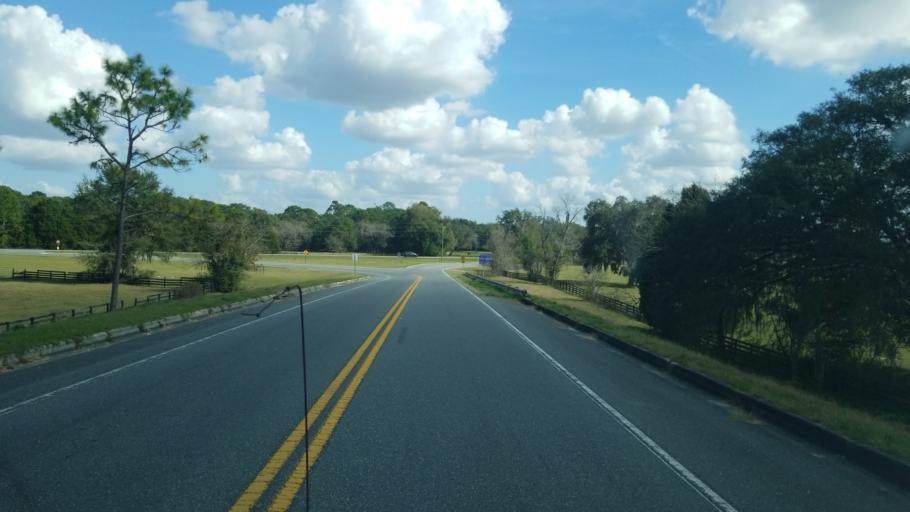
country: US
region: Florida
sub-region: Sumter County
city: Wildwood
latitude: 28.9308
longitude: -82.1108
